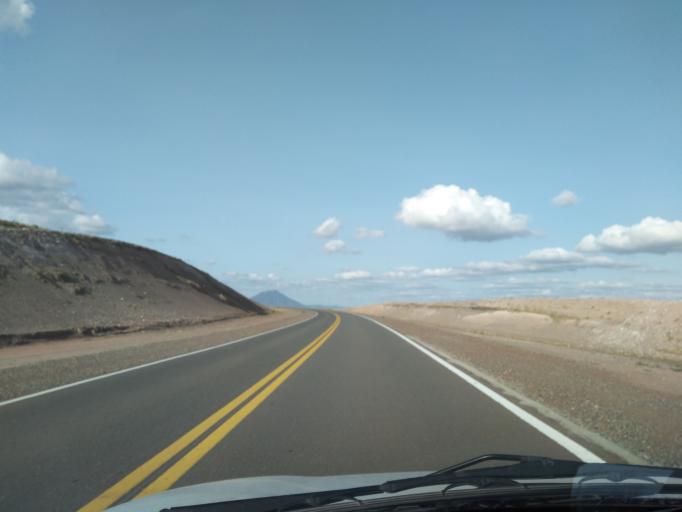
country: AR
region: Mendoza
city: Malargue
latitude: -34.8198
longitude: -69.2511
